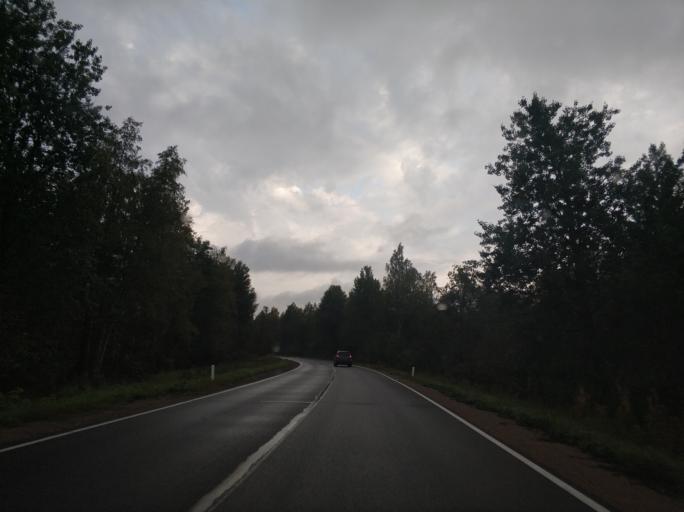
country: RU
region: Leningrad
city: Borisova Griva
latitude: 60.1323
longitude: 30.9628
